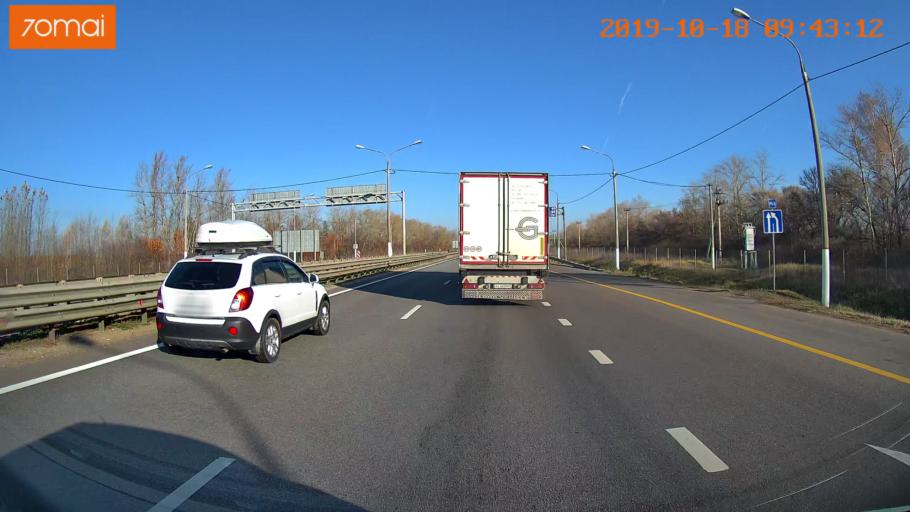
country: RU
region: Tula
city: Kazachka
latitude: 53.2945
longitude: 38.1782
